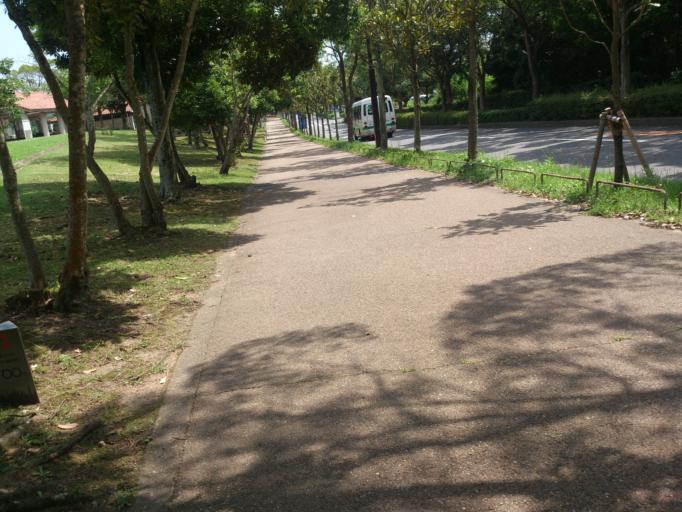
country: JP
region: Hyogo
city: Kobe
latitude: 34.7109
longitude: 135.1136
